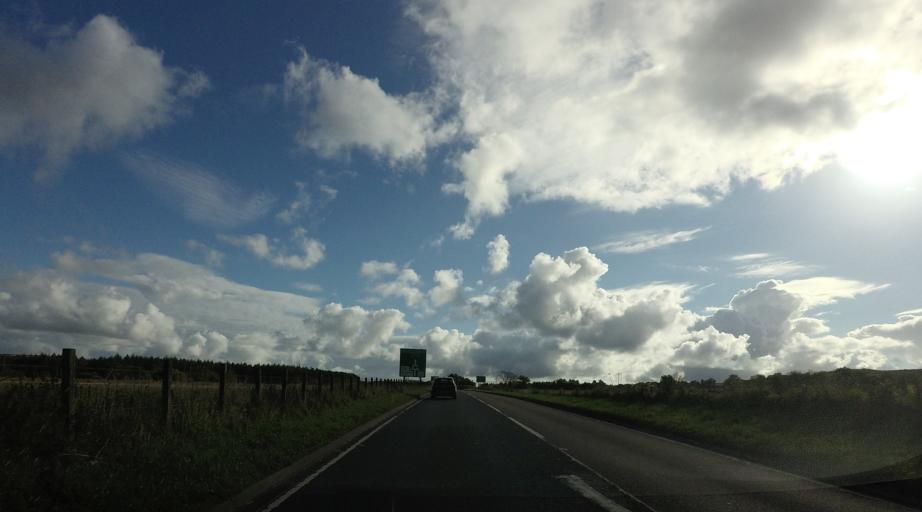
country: GB
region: Scotland
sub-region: Fife
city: Freuchie
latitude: 56.2369
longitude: -3.1554
